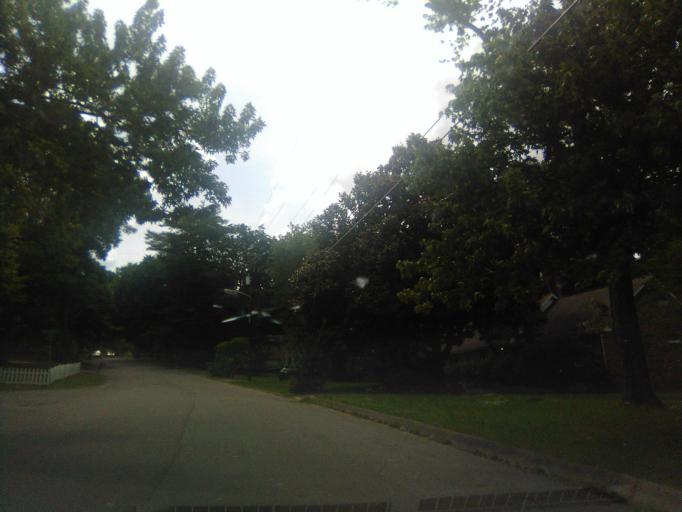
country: US
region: Tennessee
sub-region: Davidson County
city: Belle Meade
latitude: 36.0825
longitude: -86.8909
